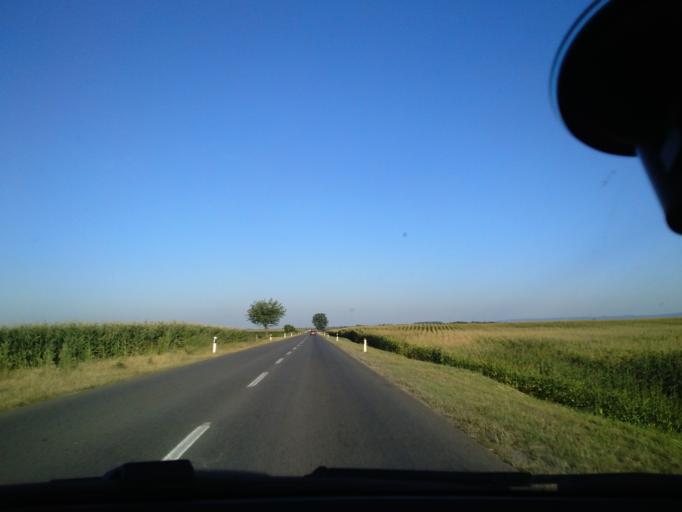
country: RS
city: Maglic
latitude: 45.3876
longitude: 19.4962
